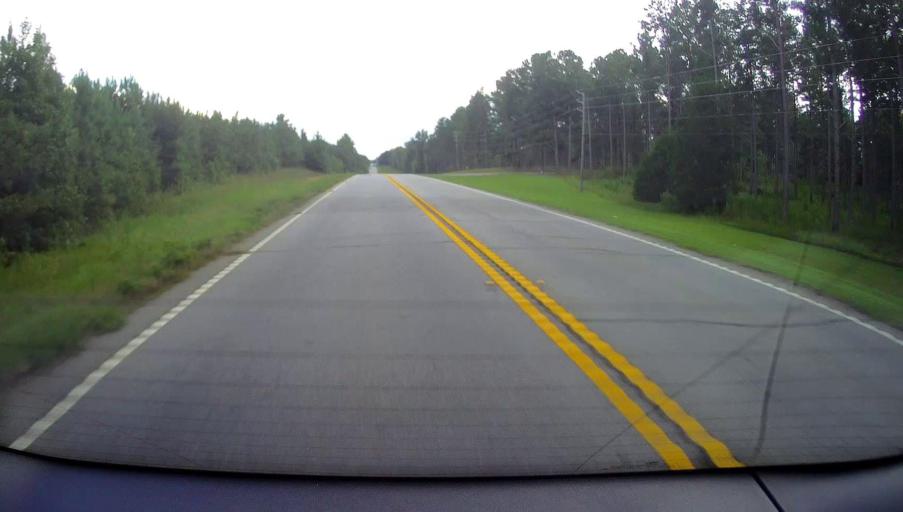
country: US
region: Georgia
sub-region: Meriwether County
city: Greenville
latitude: 33.0566
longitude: -84.5695
